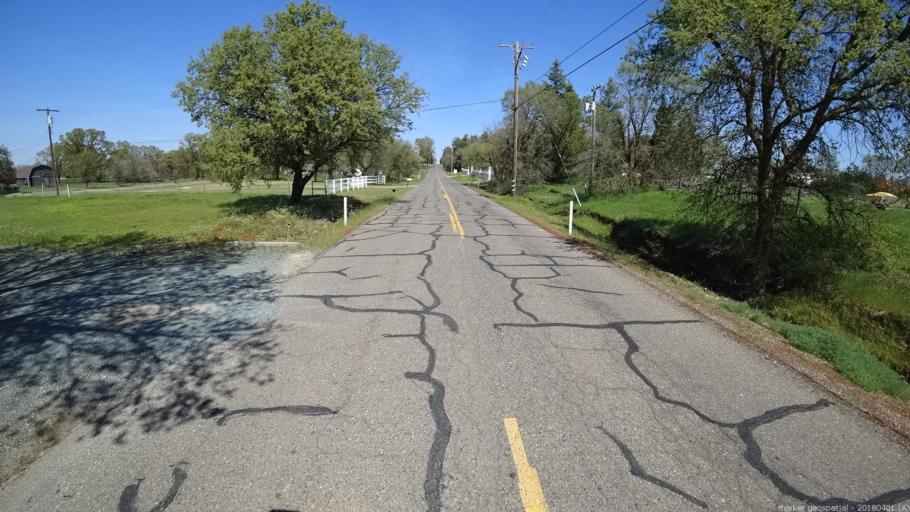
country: US
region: California
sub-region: Sacramento County
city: Wilton
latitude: 38.4171
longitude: -121.2041
